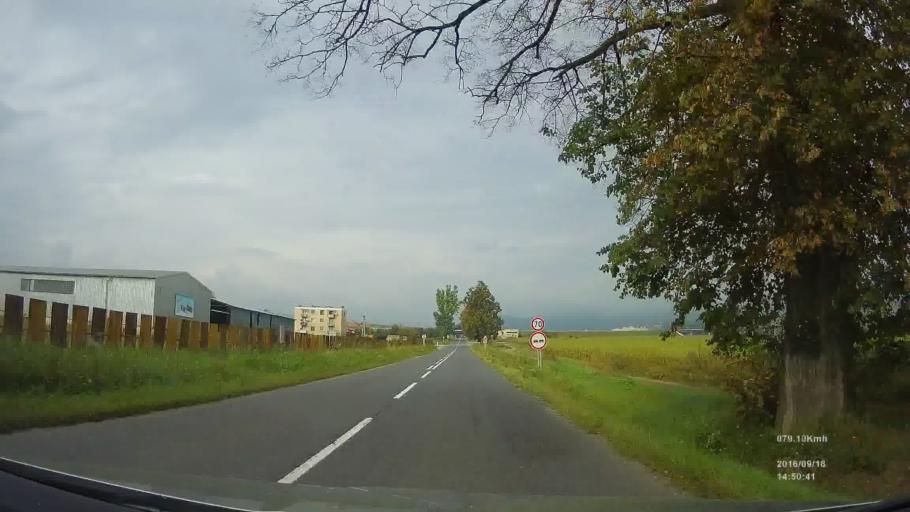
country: SK
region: Presovsky
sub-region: Okres Presov
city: Levoca
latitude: 49.0000
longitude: 20.5832
